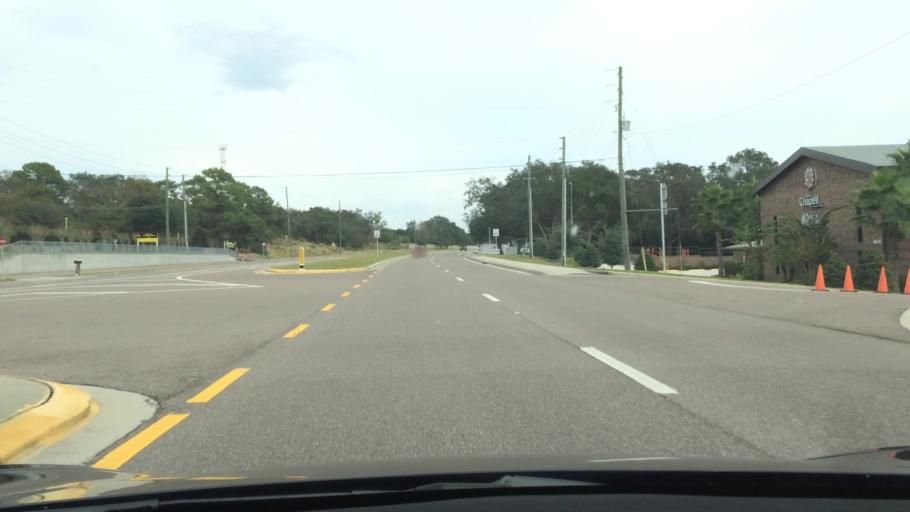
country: US
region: Florida
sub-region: Pasco County
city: Trinity
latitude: 28.1516
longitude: -82.7060
